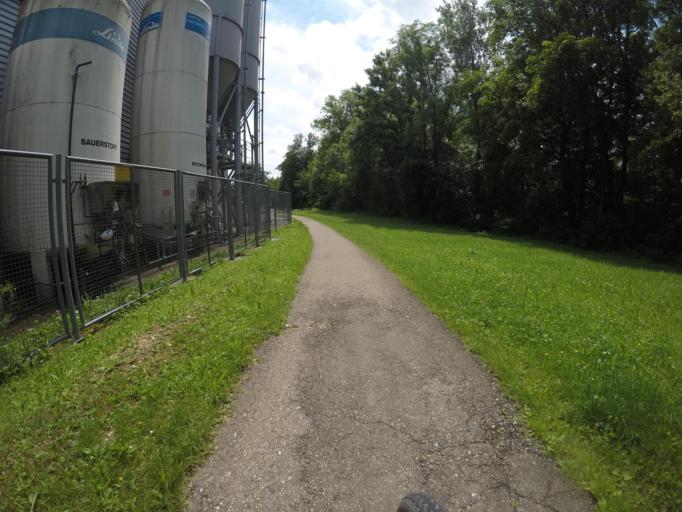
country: DE
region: Baden-Wuerttemberg
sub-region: Regierungsbezirk Stuttgart
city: Gingen an der Fils
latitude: 48.6664
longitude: 9.7756
